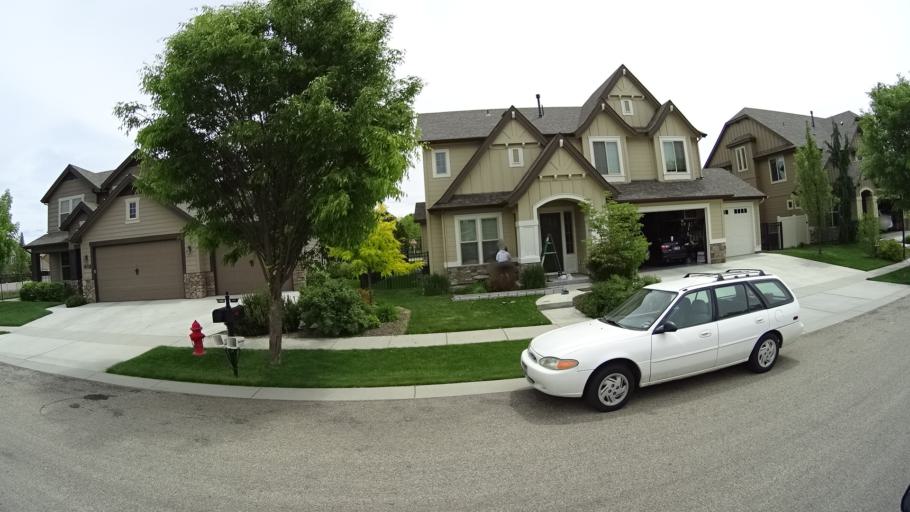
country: US
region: Idaho
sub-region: Ada County
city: Meridian
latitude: 43.5680
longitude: -116.3640
